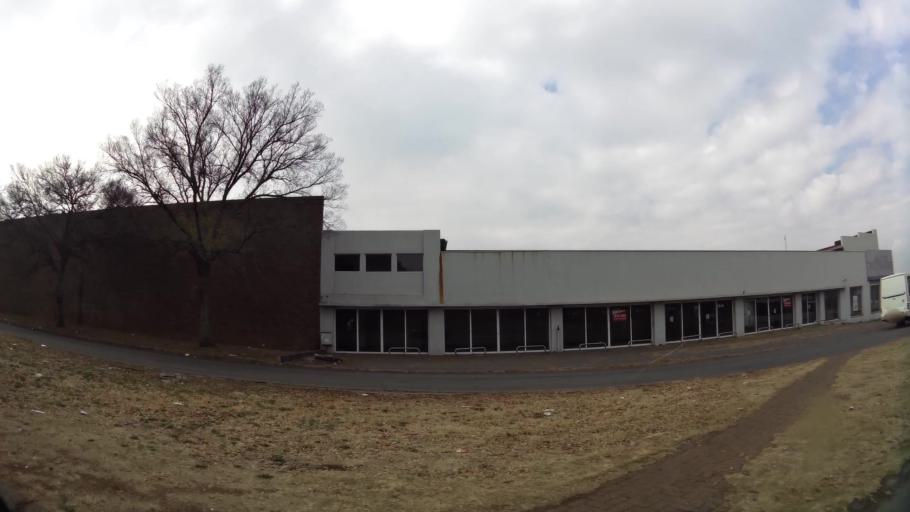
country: ZA
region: Gauteng
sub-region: Sedibeng District Municipality
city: Vanderbijlpark
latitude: -26.7046
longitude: 27.8471
